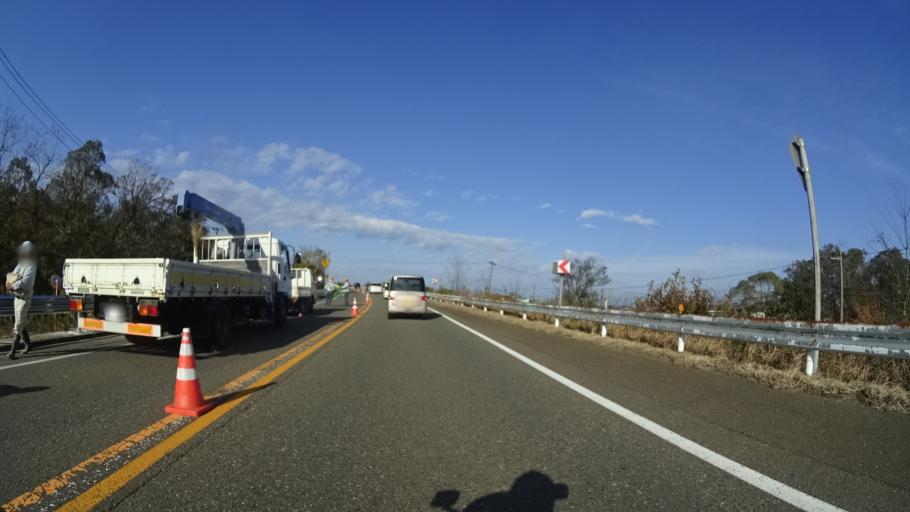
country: JP
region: Niigata
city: Joetsu
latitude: 37.2053
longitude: 138.2999
